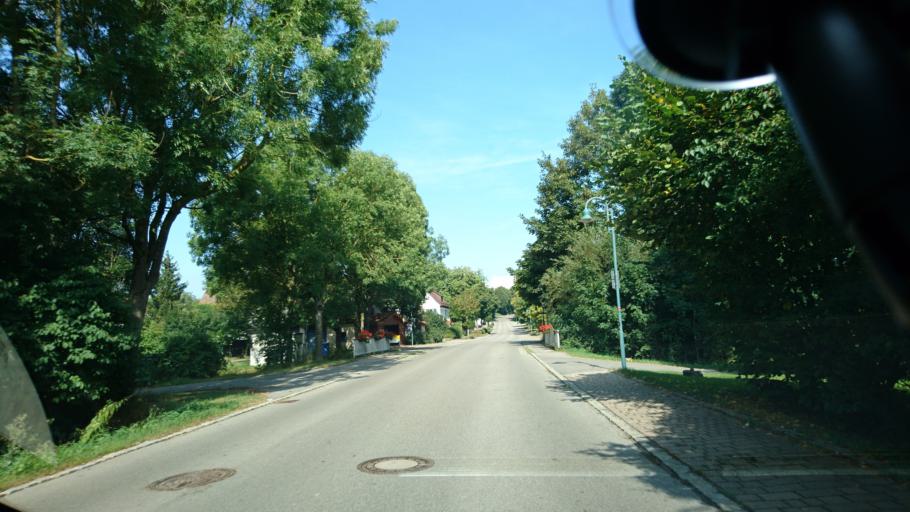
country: DE
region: Baden-Wuerttemberg
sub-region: Regierungsbezirk Stuttgart
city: Wolpertshausen
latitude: 49.1811
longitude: 9.8809
